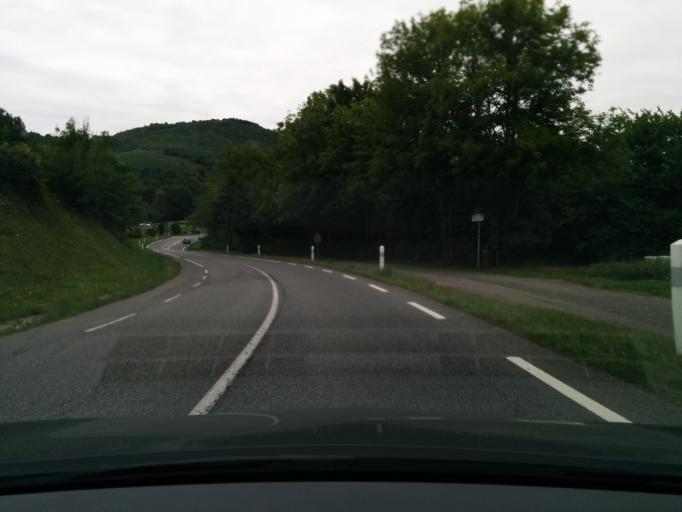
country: FR
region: Midi-Pyrenees
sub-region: Departement des Hautes-Pyrenees
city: La Barthe-de-Neste
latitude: 43.0101
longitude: 0.3743
